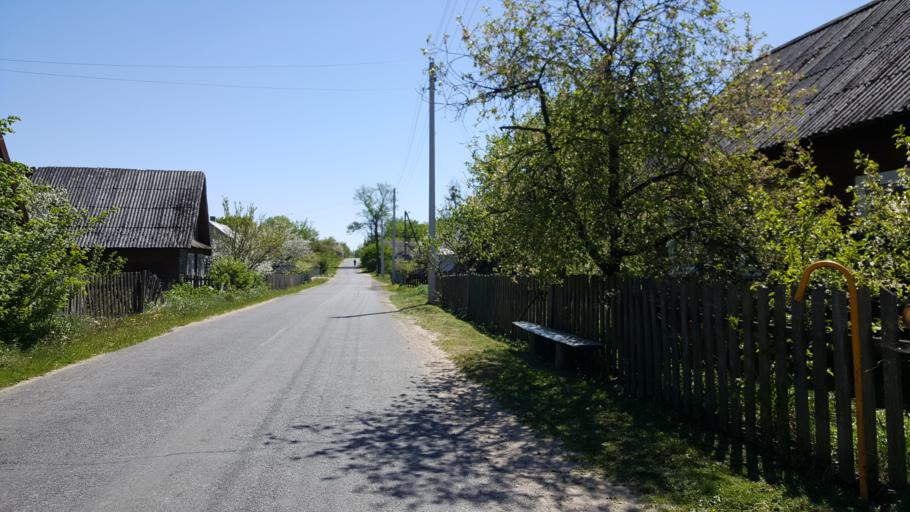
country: BY
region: Brest
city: Kamyanyuki
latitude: 52.5015
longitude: 23.7537
